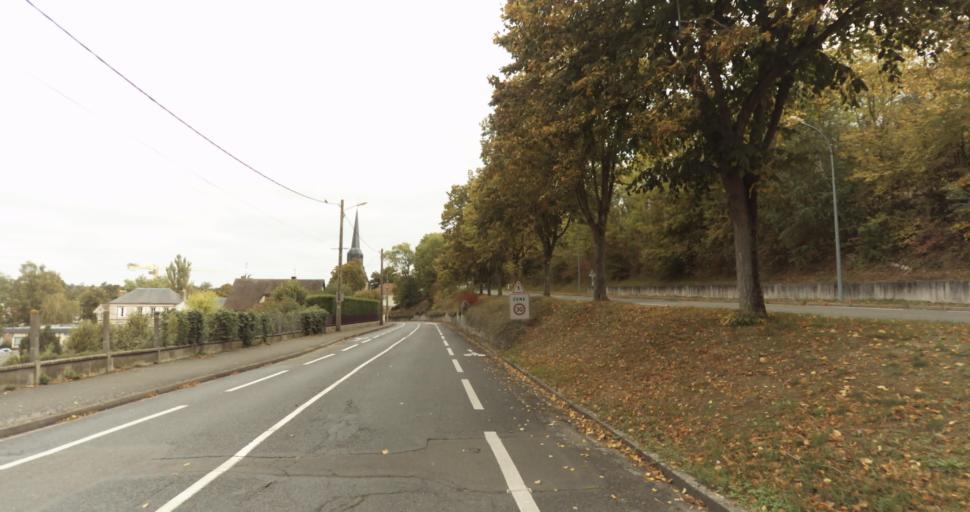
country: FR
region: Centre
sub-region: Departement d'Eure-et-Loir
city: Vernouillet
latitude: 48.7187
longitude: 1.3565
